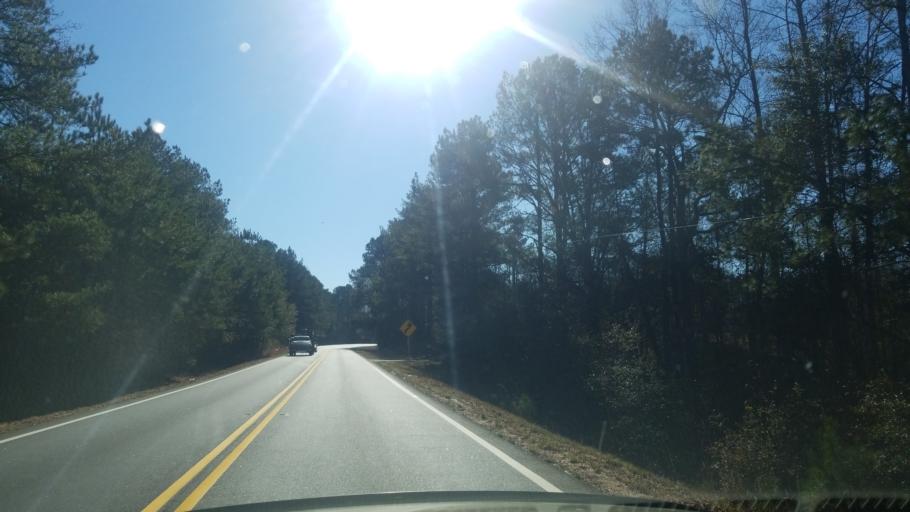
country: US
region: Alabama
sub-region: Chambers County
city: Valley
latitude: 32.8277
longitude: -85.1084
